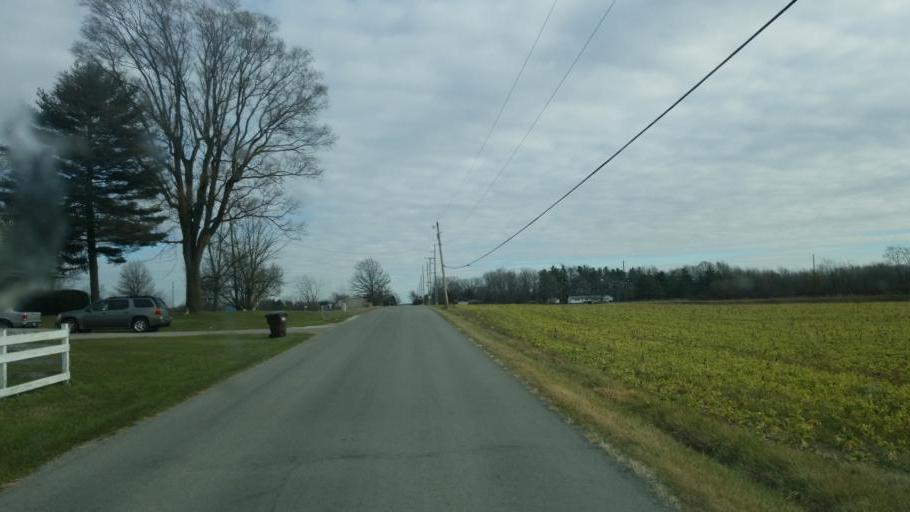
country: US
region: Ohio
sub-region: Crawford County
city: Crestline
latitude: 40.7697
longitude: -82.7504
